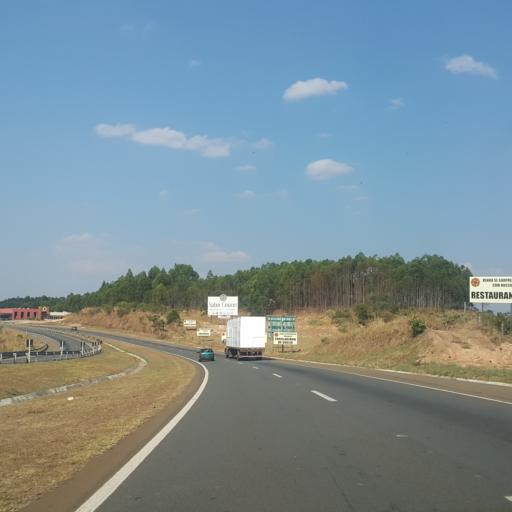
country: BR
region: Goias
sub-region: Abadiania
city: Abadiania
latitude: -16.1908
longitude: -48.6769
